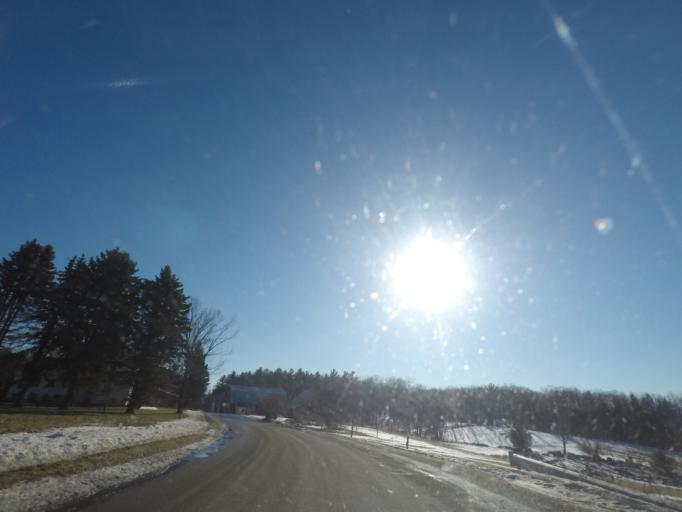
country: US
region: New York
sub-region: Rensselaer County
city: Averill Park
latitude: 42.6425
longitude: -73.5248
